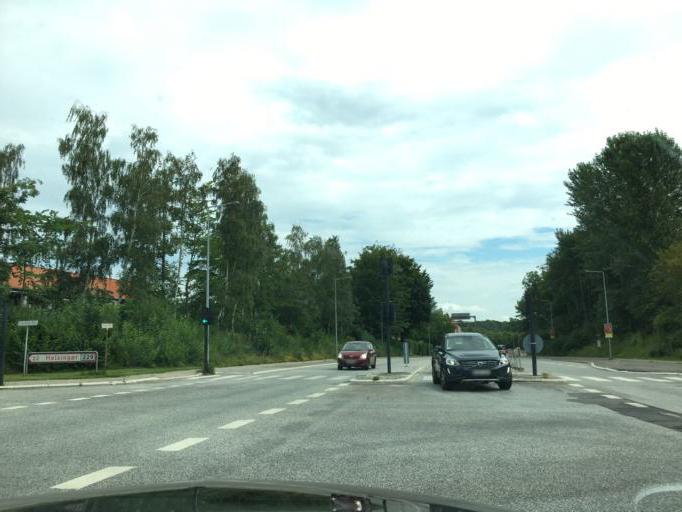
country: DK
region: Capital Region
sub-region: Horsholm Kommune
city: Horsholm
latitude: 55.8780
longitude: 12.4943
